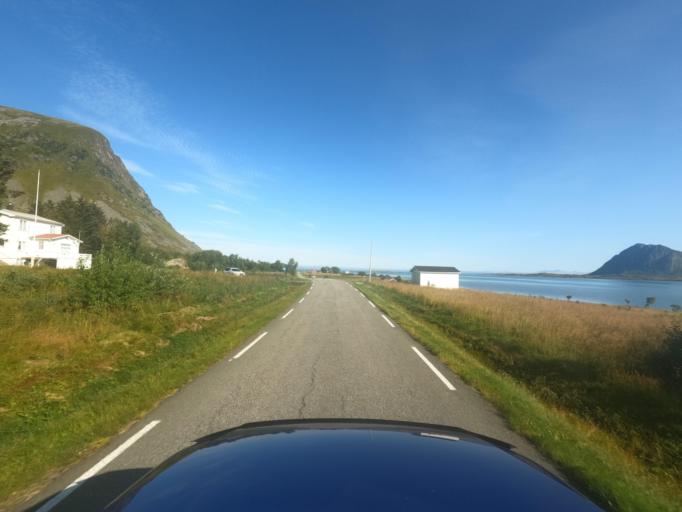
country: NO
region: Nordland
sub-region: Vestvagoy
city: Evjen
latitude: 68.3056
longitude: 14.0162
